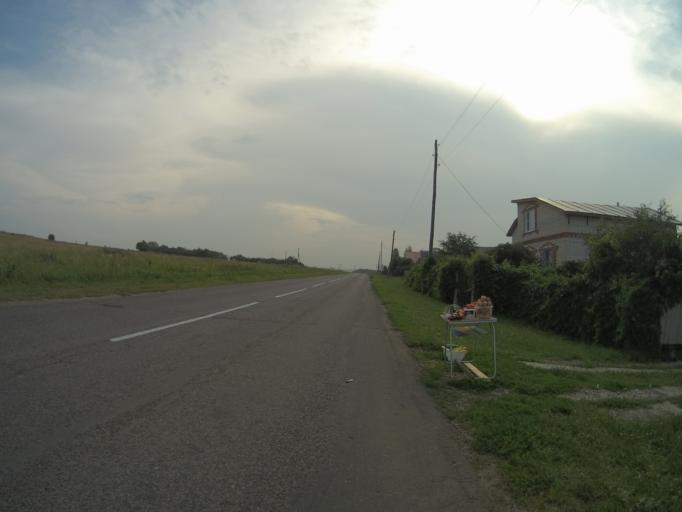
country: RU
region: Vladimir
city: Suzdal'
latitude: 56.4010
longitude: 40.3338
